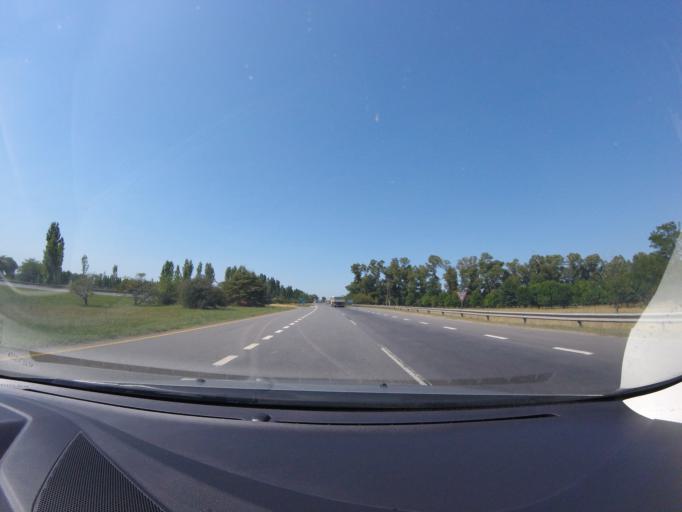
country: AR
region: Buenos Aires
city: Canuelas
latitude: -35.1370
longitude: -58.7395
